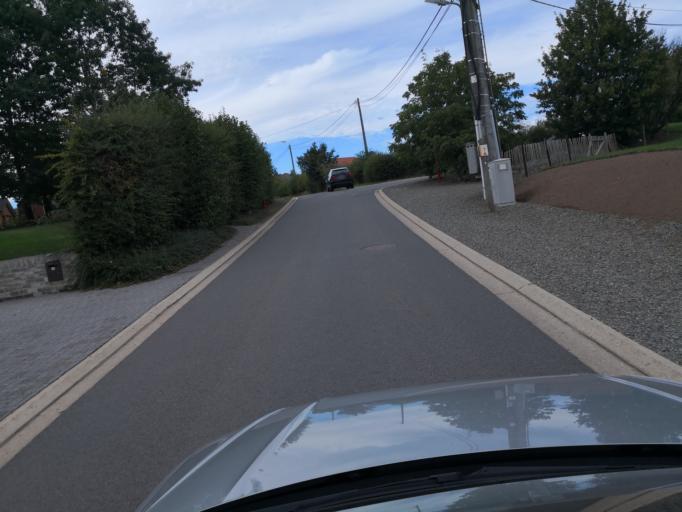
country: BE
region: Wallonia
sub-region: Province de Liege
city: Jalhay
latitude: 50.5672
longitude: 5.9437
